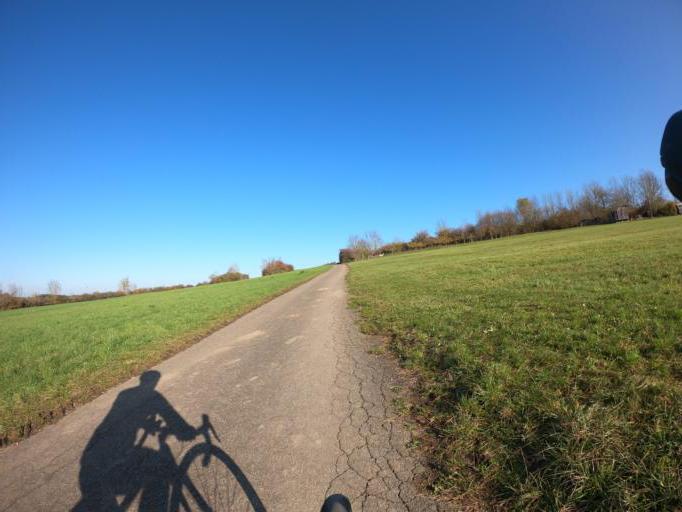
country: DE
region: Baden-Wuerttemberg
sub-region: Regierungsbezirk Stuttgart
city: Weil der Stadt
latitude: 48.7312
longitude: 8.8954
